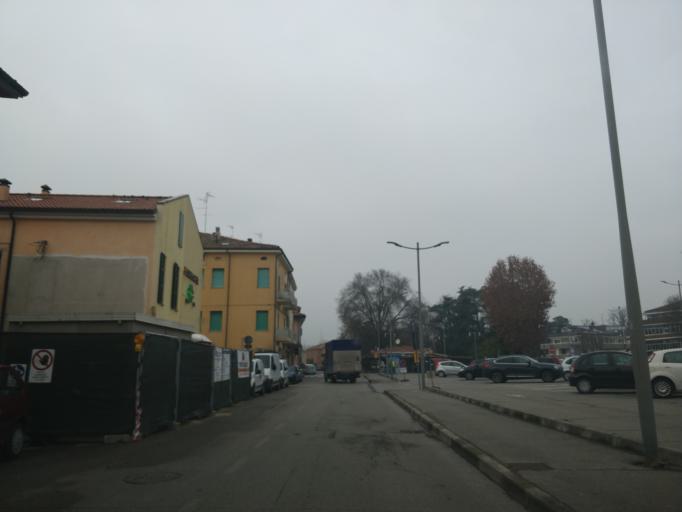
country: IT
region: Emilia-Romagna
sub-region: Provincia di Ferrara
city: Cento
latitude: 44.7288
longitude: 11.2934
